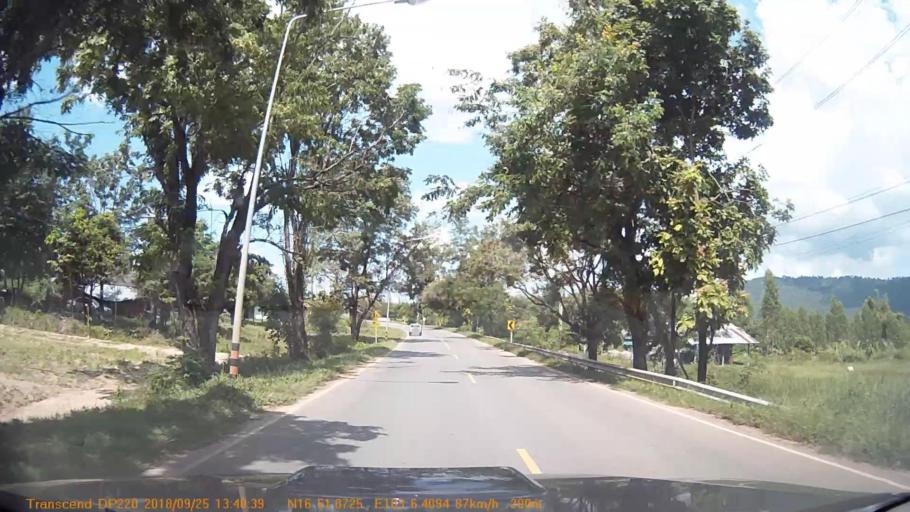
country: TH
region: Changwat Udon Thani
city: Si That
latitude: 16.8645
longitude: 103.1067
